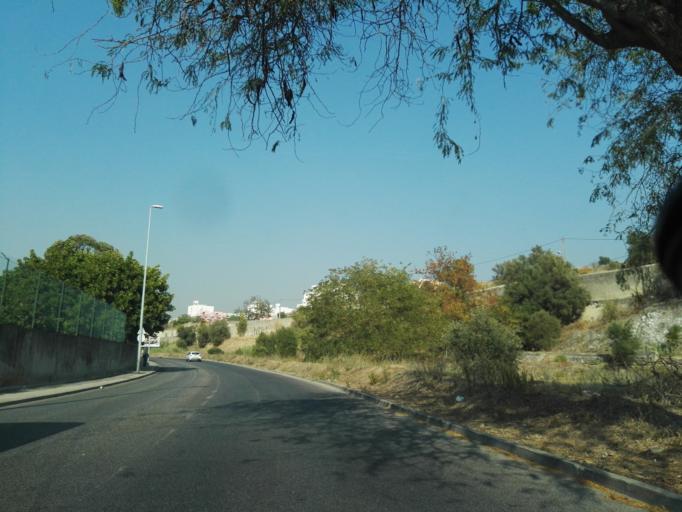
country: PT
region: Lisbon
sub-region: Lisbon
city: Lisbon
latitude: 38.7402
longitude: -9.1174
